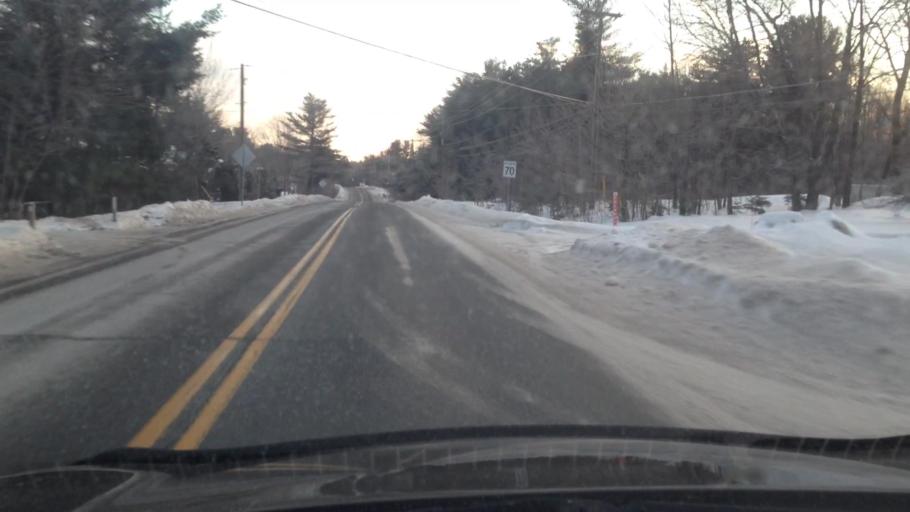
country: CA
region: Quebec
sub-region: Lanaudiere
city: Sainte-Julienne
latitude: 45.9524
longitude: -73.7342
